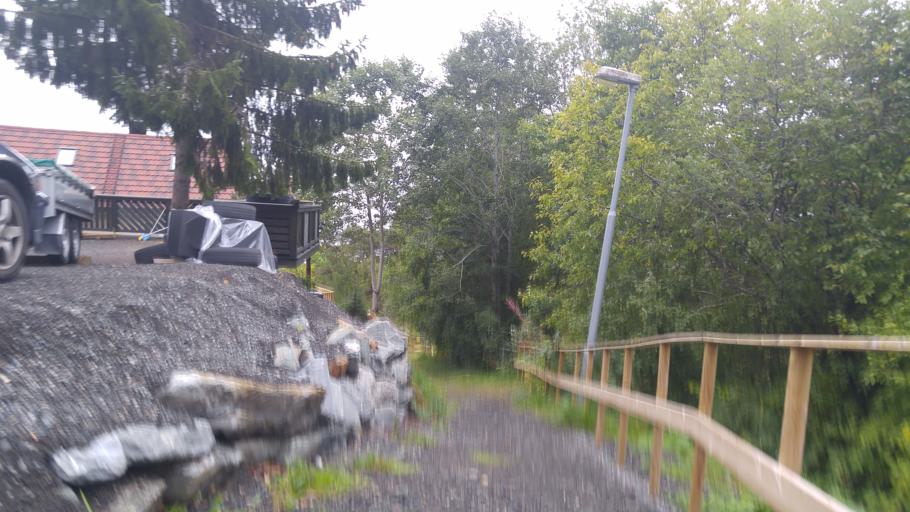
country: NO
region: Sor-Trondelag
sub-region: Trondheim
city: Trondheim
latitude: 63.4507
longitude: 10.3085
